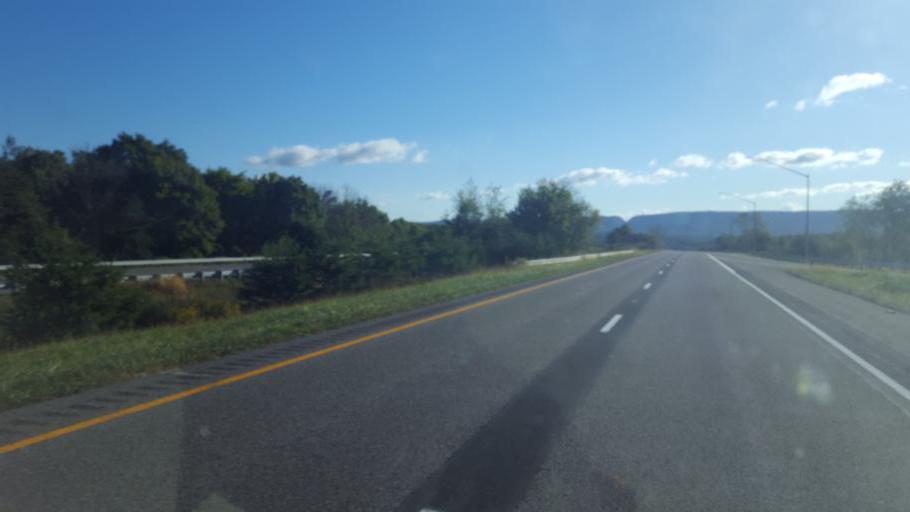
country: US
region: West Virginia
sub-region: Morgan County
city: Berkeley Springs
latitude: 39.7003
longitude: -78.3790
